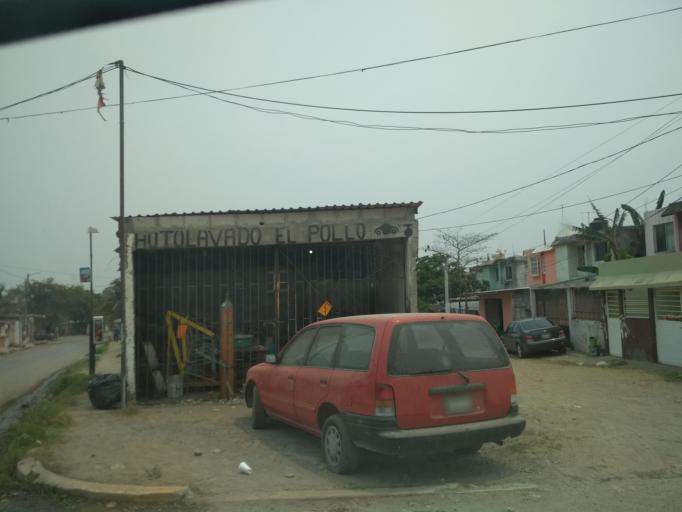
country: MX
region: Veracruz
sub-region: Veracruz
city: Colonia Chalchihuecan
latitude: 19.2113
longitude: -96.2145
